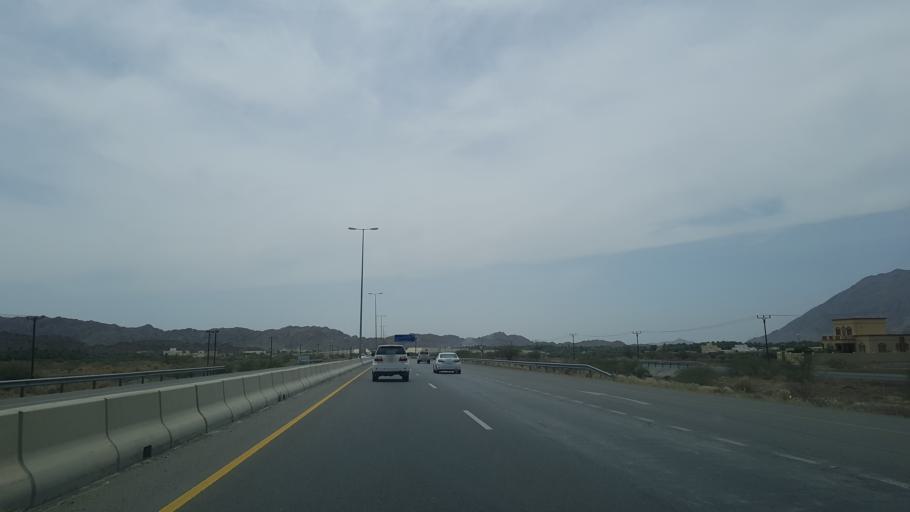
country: OM
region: Muhafazat ad Dakhiliyah
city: Izki
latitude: 23.0079
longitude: 57.7914
